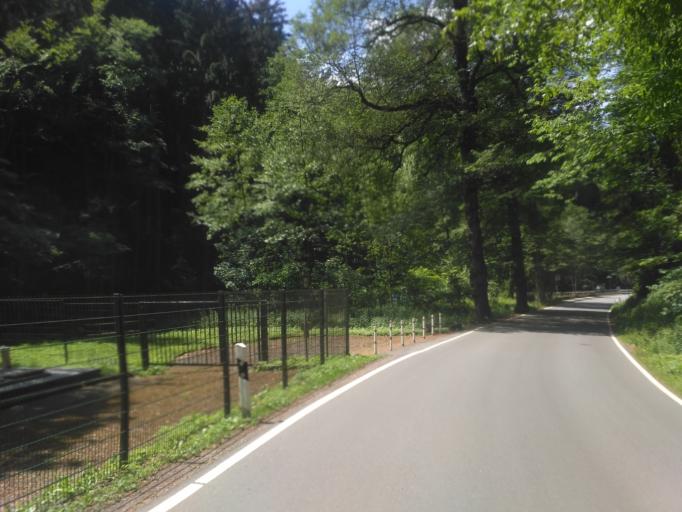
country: DE
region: Saxony
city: Sebnitz
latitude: 50.9238
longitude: 14.2867
